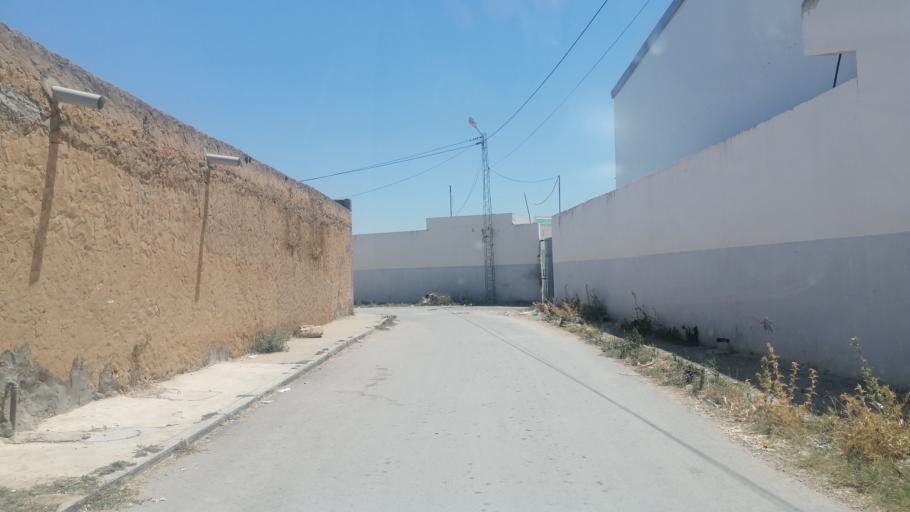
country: TN
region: Al Qayrawan
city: Sbikha
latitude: 36.1248
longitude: 10.0904
